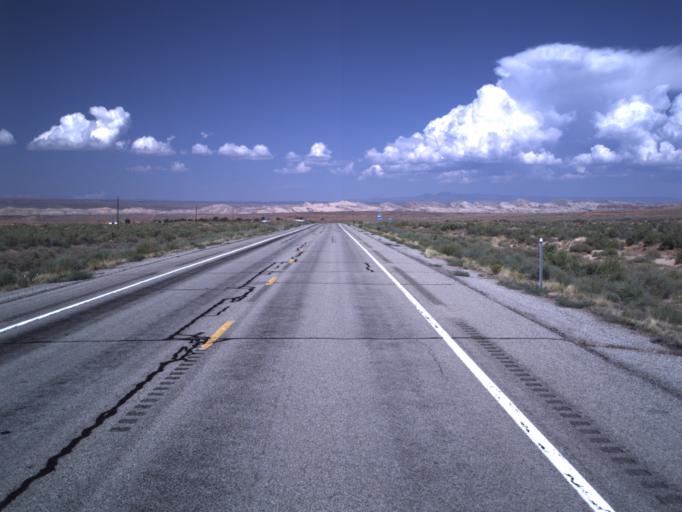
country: US
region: Utah
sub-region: San Juan County
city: Blanding
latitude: 37.1979
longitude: -109.6016
